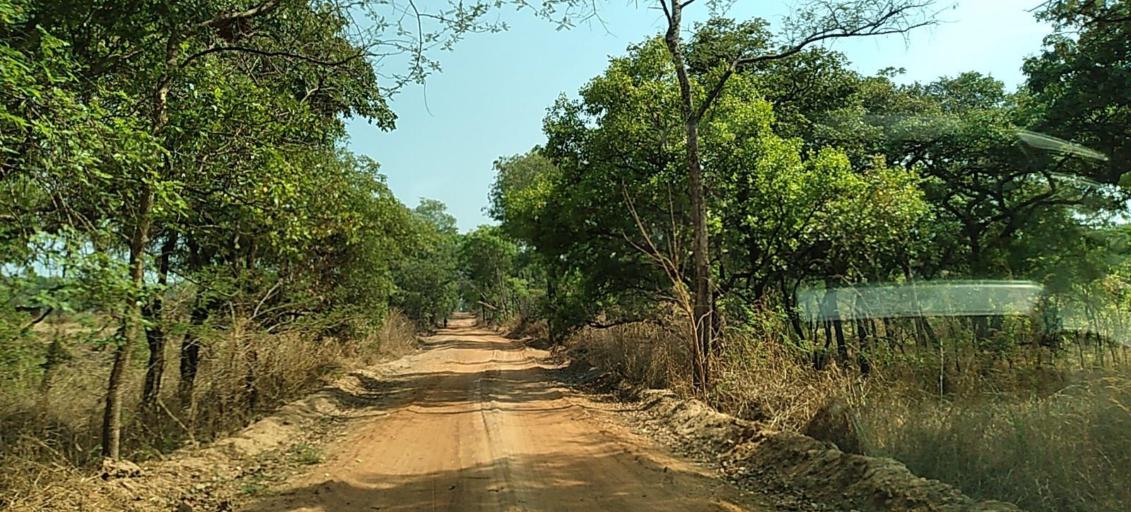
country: ZM
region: Copperbelt
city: Kalulushi
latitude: -12.9169
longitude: 27.8227
